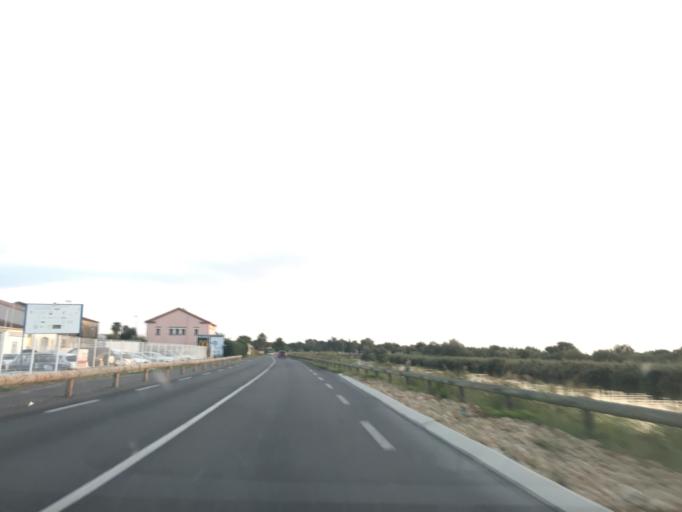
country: FR
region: Languedoc-Roussillon
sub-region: Departement du Gard
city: Aigues-Mortes
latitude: 43.5638
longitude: 4.1858
